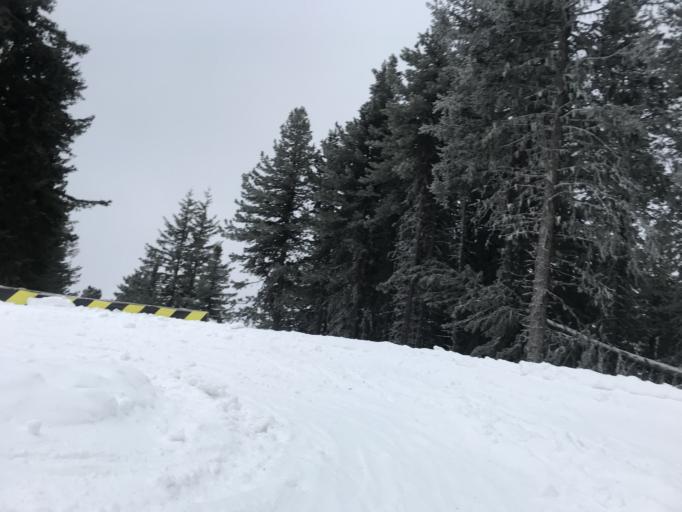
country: IT
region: Trentino-Alto Adige
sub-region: Bolzano
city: San Pietro
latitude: 46.6886
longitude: 11.7071
